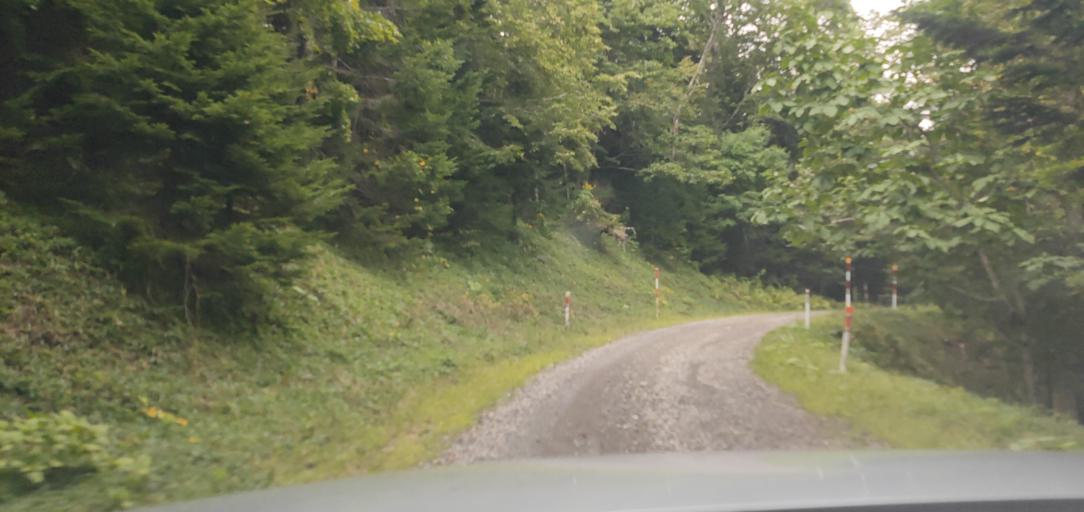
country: JP
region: Hokkaido
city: Kitami
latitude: 43.3678
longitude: 143.9364
